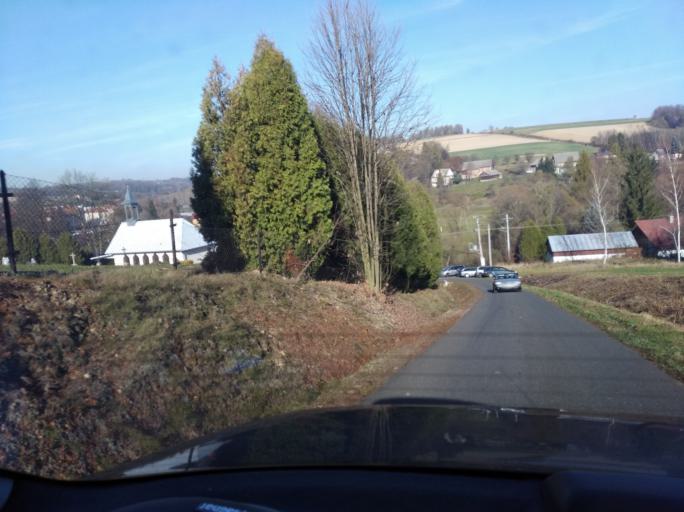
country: PL
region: Subcarpathian Voivodeship
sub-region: Powiat ropczycko-sedziszowski
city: Wielopole Skrzynskie
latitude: 49.9285
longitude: 21.5556
